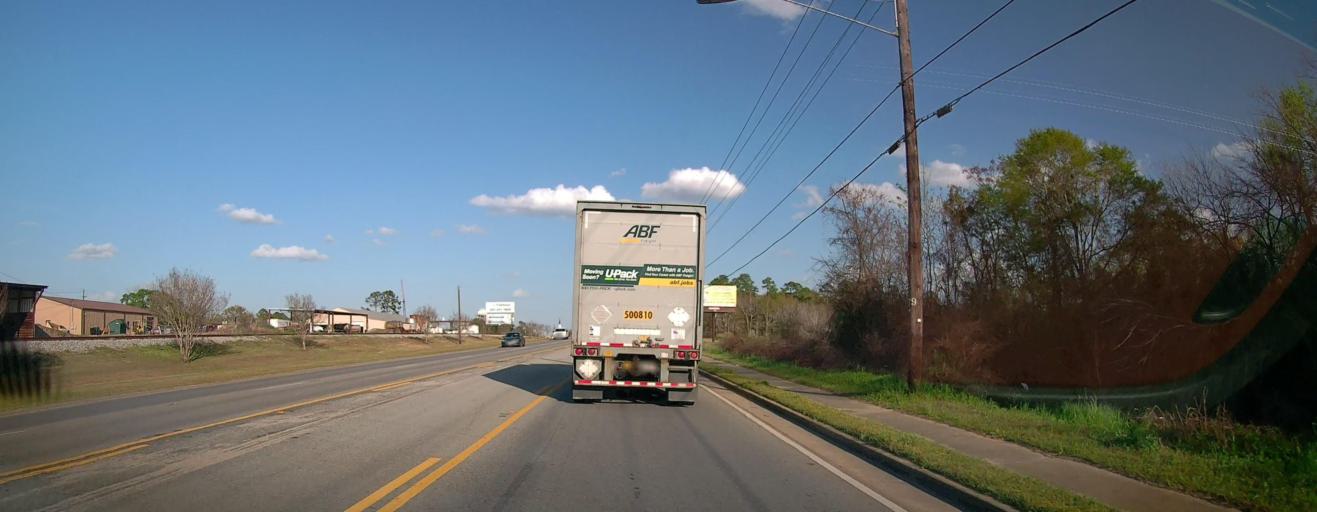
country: US
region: Georgia
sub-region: Toombs County
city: Lyons
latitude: 32.2018
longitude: -82.3340
